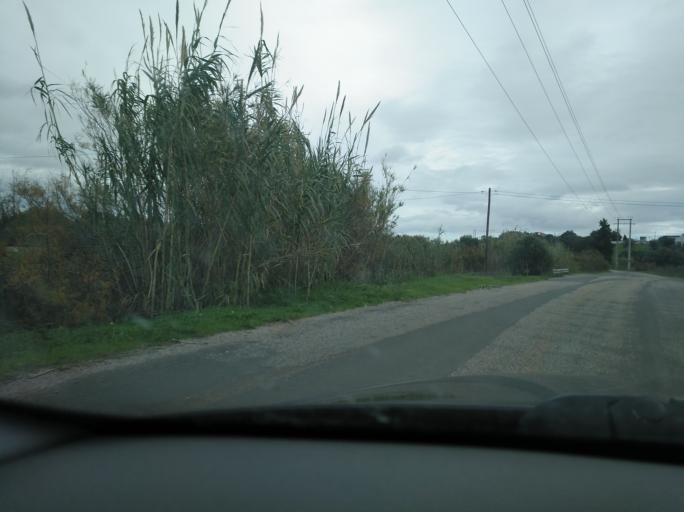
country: PT
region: Faro
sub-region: Vila Real de Santo Antonio
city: Monte Gordo
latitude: 37.1974
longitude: -7.4876
